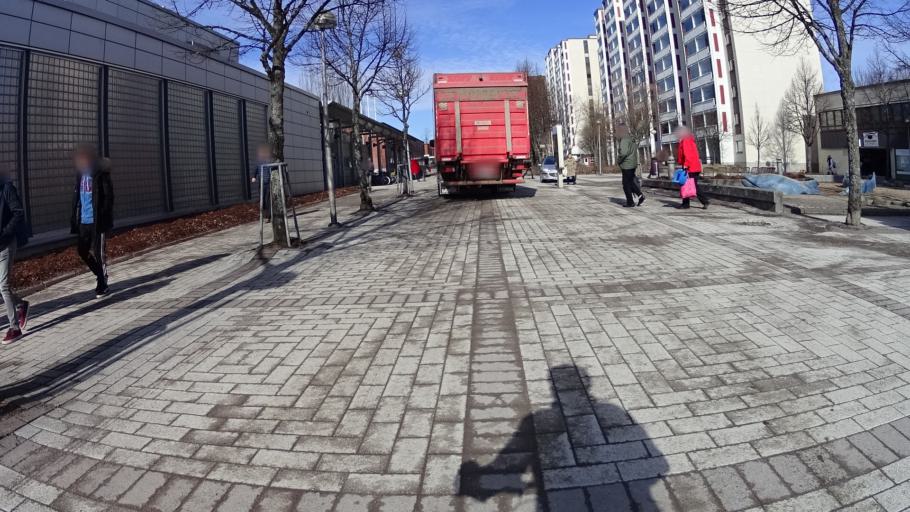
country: FI
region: Uusimaa
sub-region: Helsinki
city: Teekkarikylae
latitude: 60.2651
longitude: 24.8520
